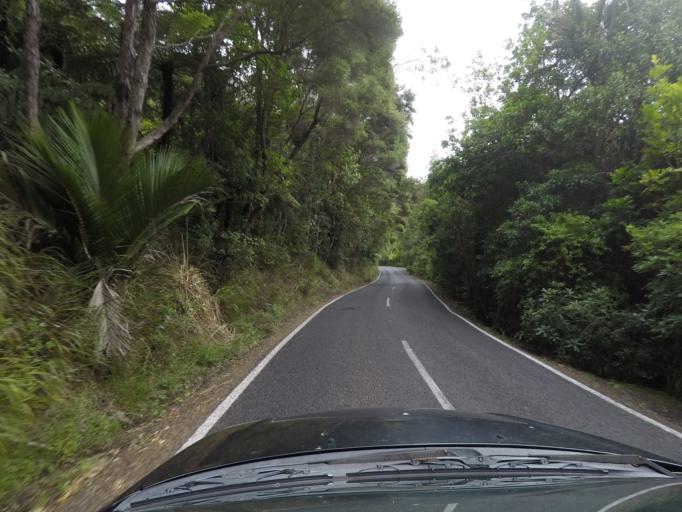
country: NZ
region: Auckland
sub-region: Auckland
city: Titirangi
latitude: -36.9469
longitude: 174.6589
